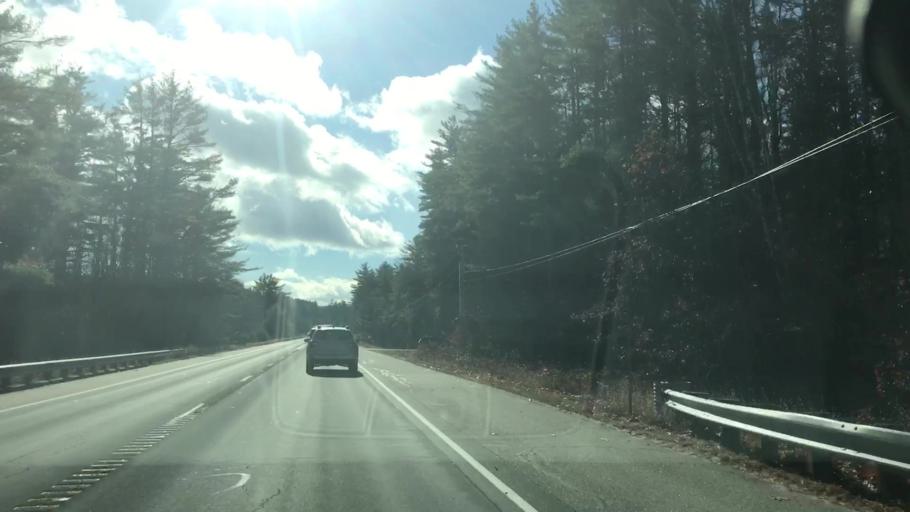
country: US
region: New Hampshire
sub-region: Carroll County
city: Wolfeboro
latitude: 43.5348
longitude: -71.2037
